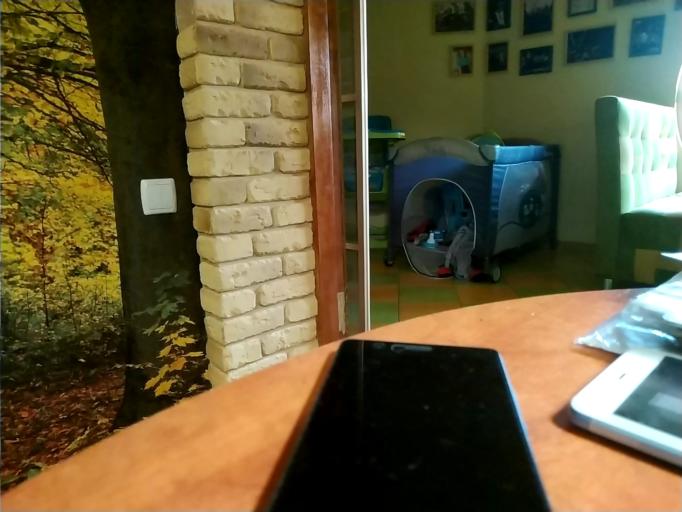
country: RU
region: Kaluga
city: Duminichi
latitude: 53.7213
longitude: 35.4233
